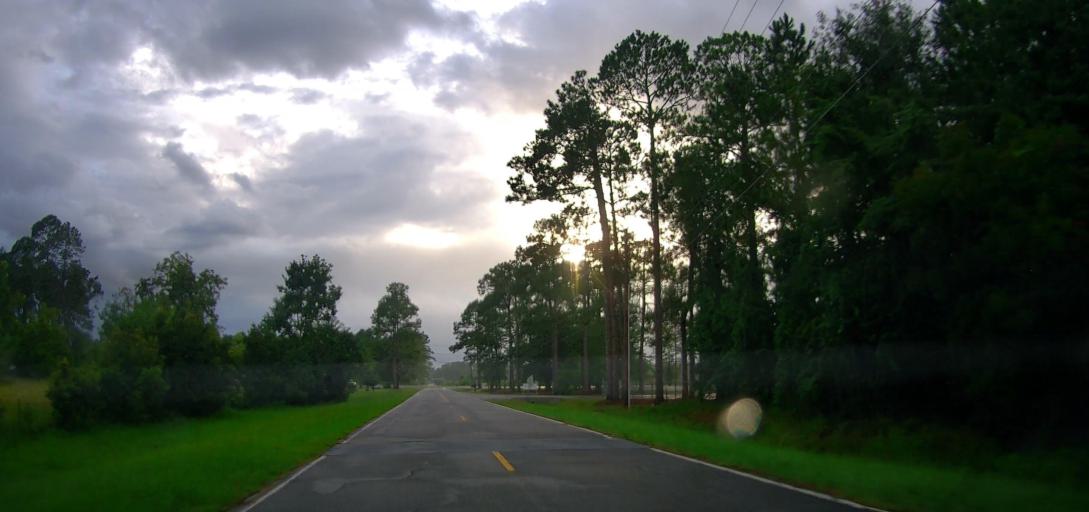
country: US
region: Georgia
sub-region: Ware County
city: Deenwood
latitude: 31.1948
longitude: -82.3993
